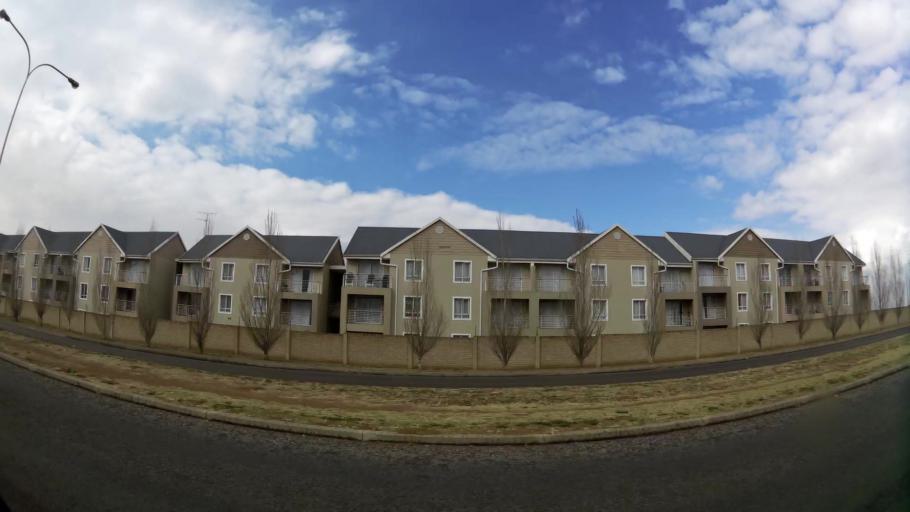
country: ZA
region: Gauteng
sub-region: Sedibeng District Municipality
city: Vanderbijlpark
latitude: -26.7183
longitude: 27.8850
